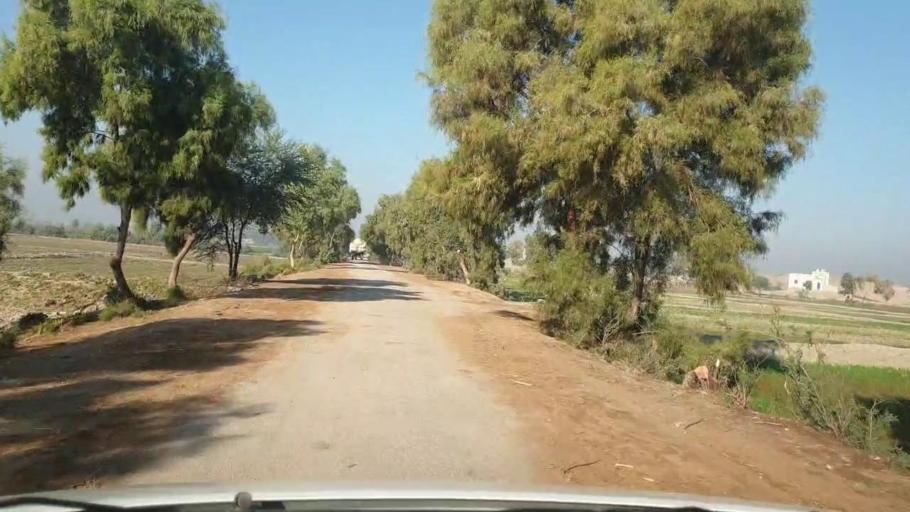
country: PK
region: Sindh
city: Dadu
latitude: 26.6755
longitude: 67.8362
